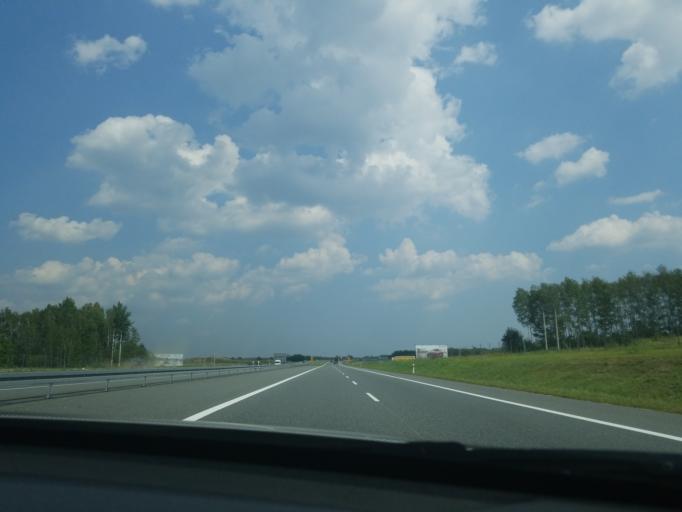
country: PL
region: Lesser Poland Voivodeship
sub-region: Powiat tarnowski
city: Lisia Gora
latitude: 50.0581
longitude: 21.0362
